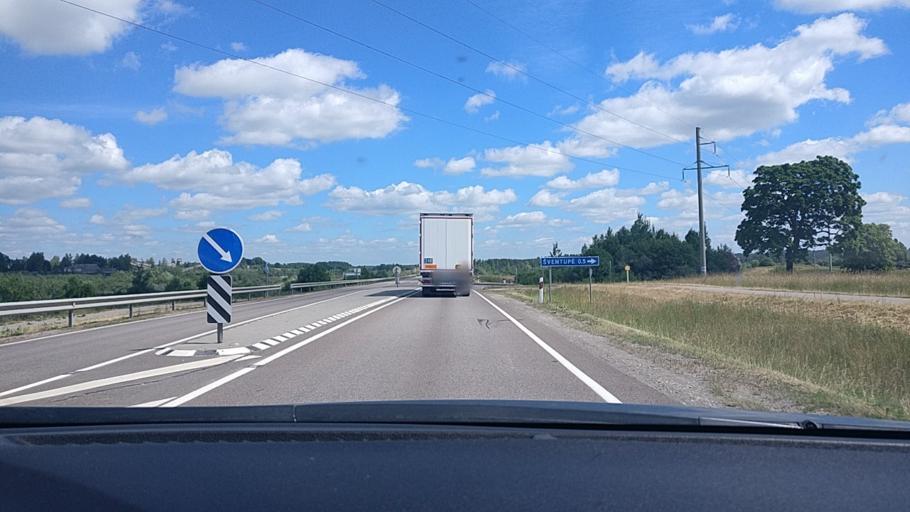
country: LT
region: Vilnius County
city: Ukmerge
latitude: 55.3230
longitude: 24.8785
